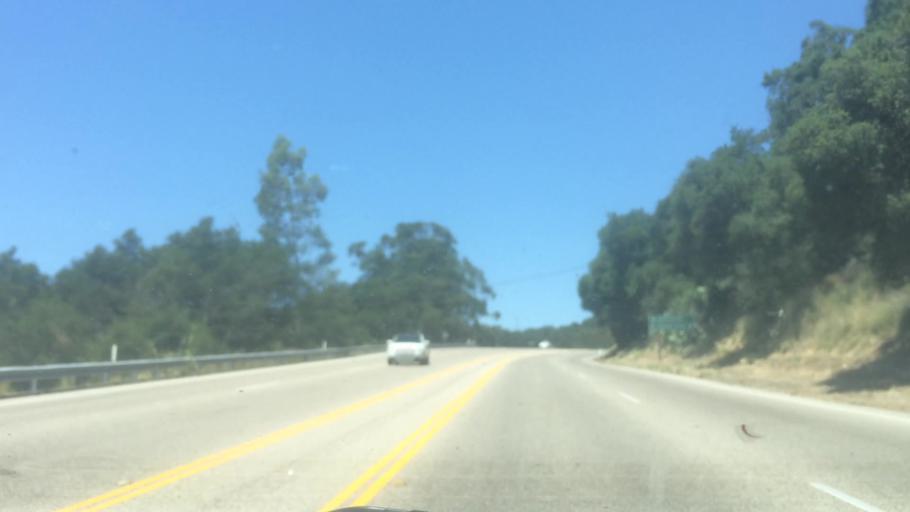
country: US
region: California
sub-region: Santa Barbara County
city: Goleta
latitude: 34.5087
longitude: -119.8208
